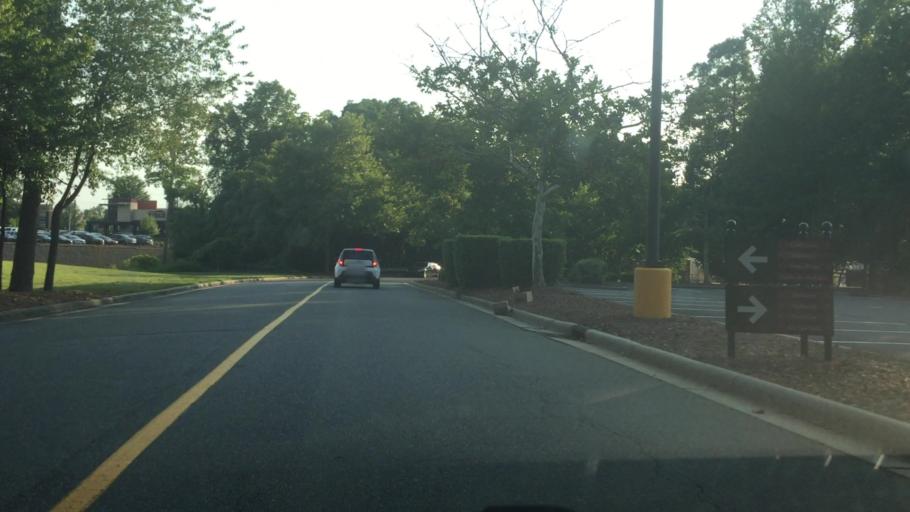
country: US
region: North Carolina
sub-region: Iredell County
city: Mooresville
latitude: 35.5969
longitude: -80.8700
